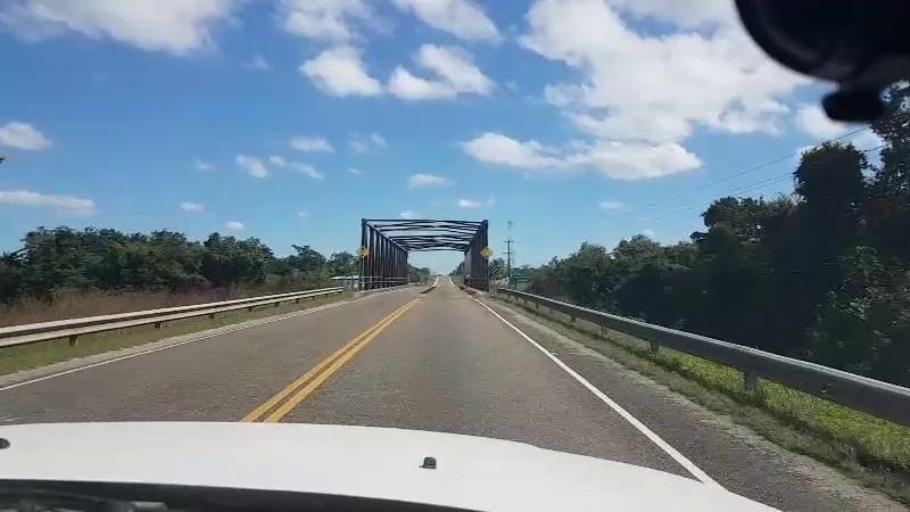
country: BZ
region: Cayo
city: Belmopan
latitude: 17.2771
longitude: -88.6672
